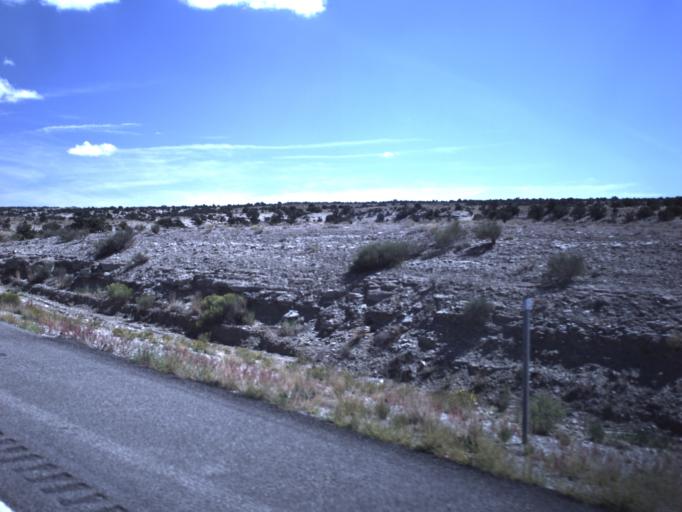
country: US
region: Utah
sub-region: Emery County
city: Ferron
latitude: 38.8432
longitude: -110.9731
